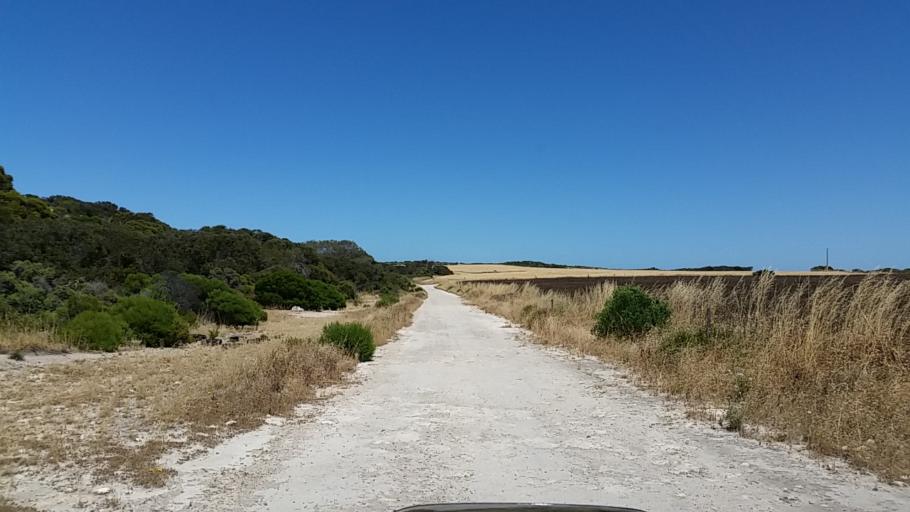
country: AU
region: South Australia
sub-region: Yorke Peninsula
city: Honiton
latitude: -35.2349
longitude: 137.1134
